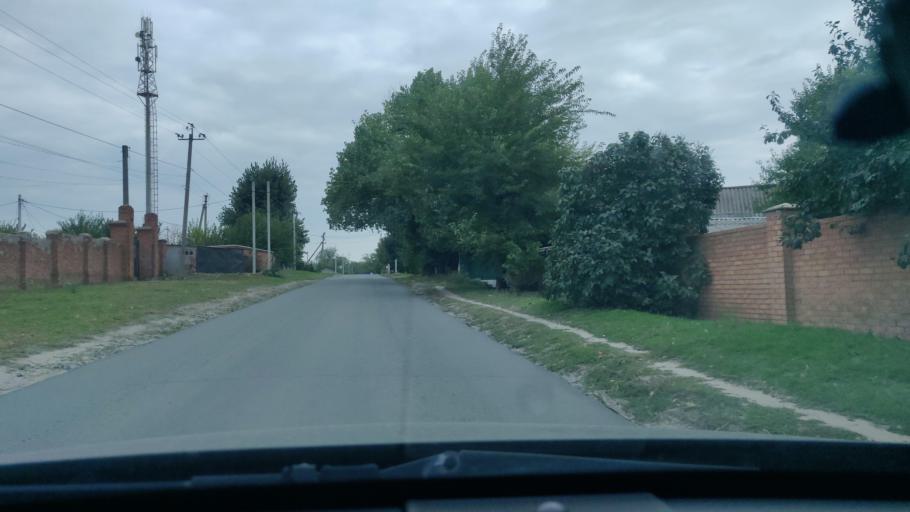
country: RU
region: Rostov
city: Ust'-Donetskiy
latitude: 47.6473
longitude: 40.8647
